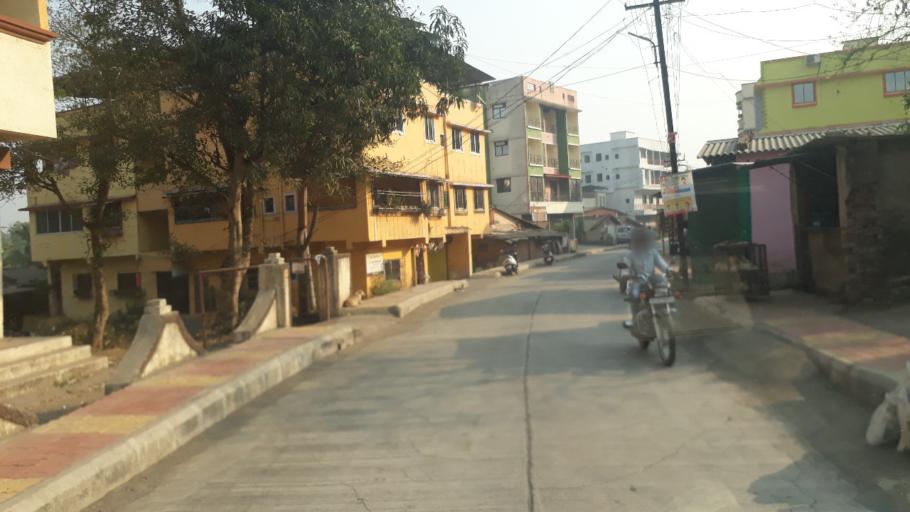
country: IN
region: Maharashtra
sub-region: Raigarh
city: Neral
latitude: 19.0216
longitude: 73.3125
